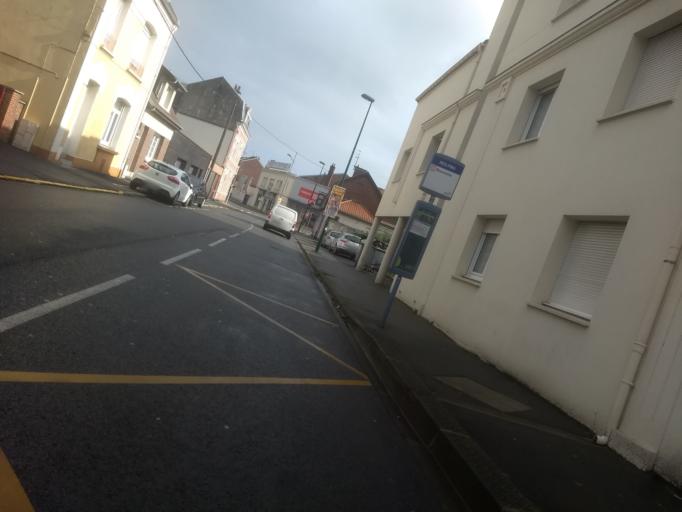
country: FR
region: Nord-Pas-de-Calais
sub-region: Departement du Pas-de-Calais
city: Arras
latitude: 50.2781
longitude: 2.7809
